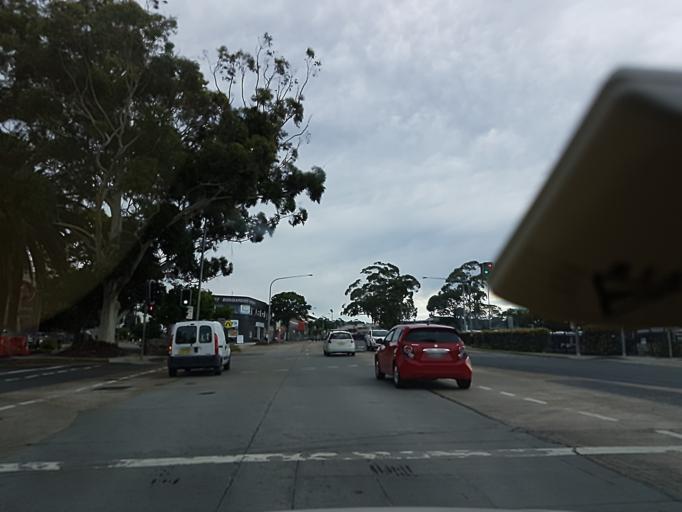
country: AU
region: New South Wales
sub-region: Warringah
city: Brookvale
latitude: -33.7663
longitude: 151.2694
